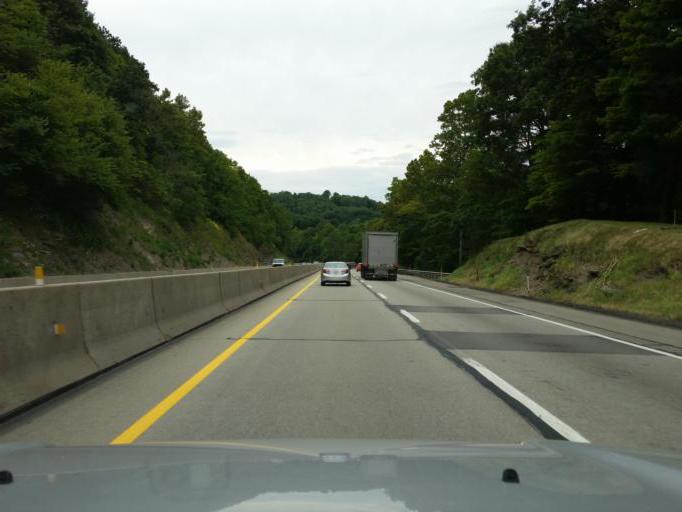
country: US
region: Pennsylvania
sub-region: Westmoreland County
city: Level Green
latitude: 40.4159
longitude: -79.7307
